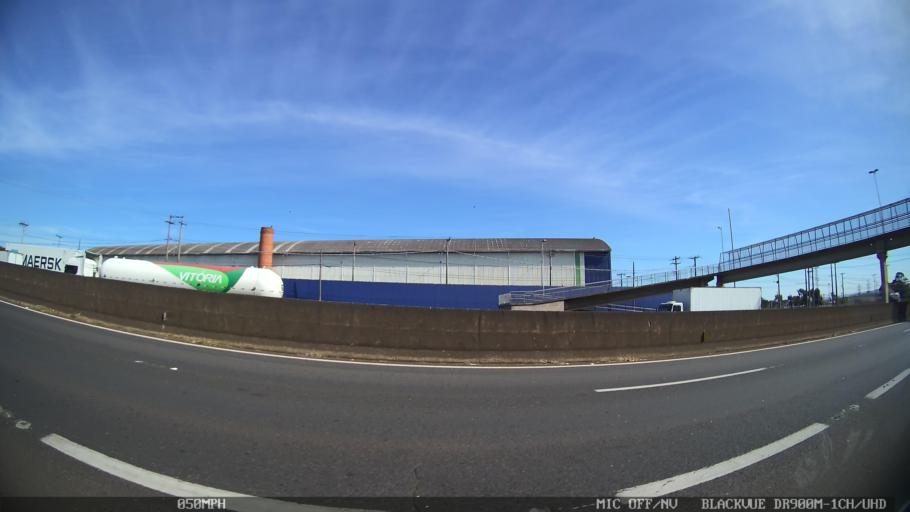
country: BR
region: Sao Paulo
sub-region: Porto Ferreira
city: Porto Ferreira
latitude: -21.8538
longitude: -47.4948
